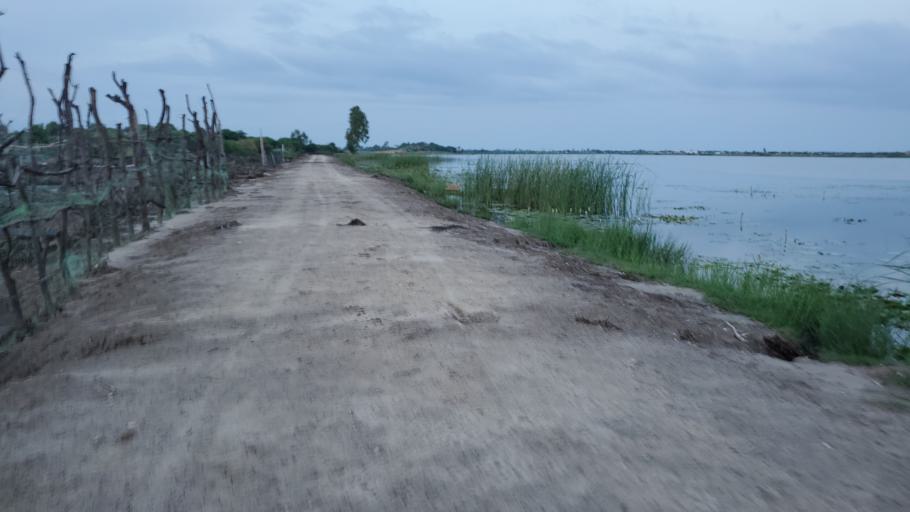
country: SN
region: Saint-Louis
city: Saint-Louis
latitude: 16.0486
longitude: -16.4141
